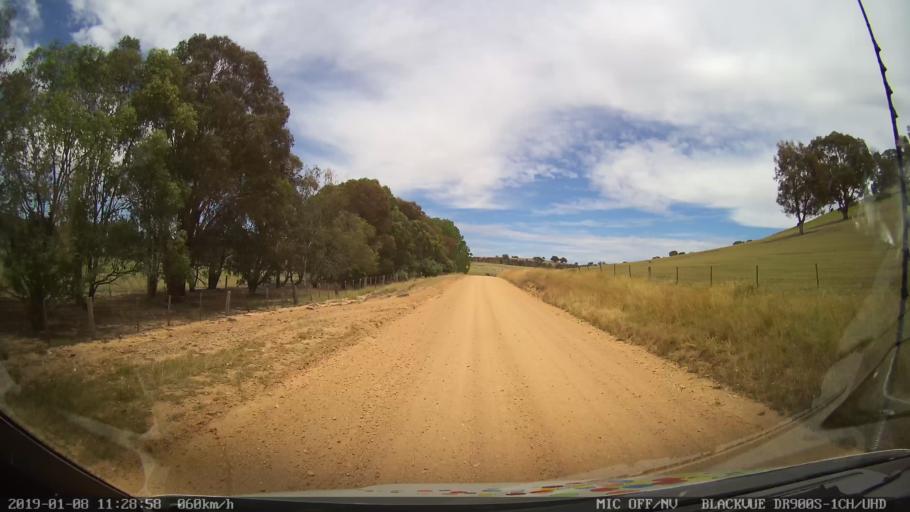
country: AU
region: New South Wales
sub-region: Guyra
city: Guyra
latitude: -30.2987
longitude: 151.5511
